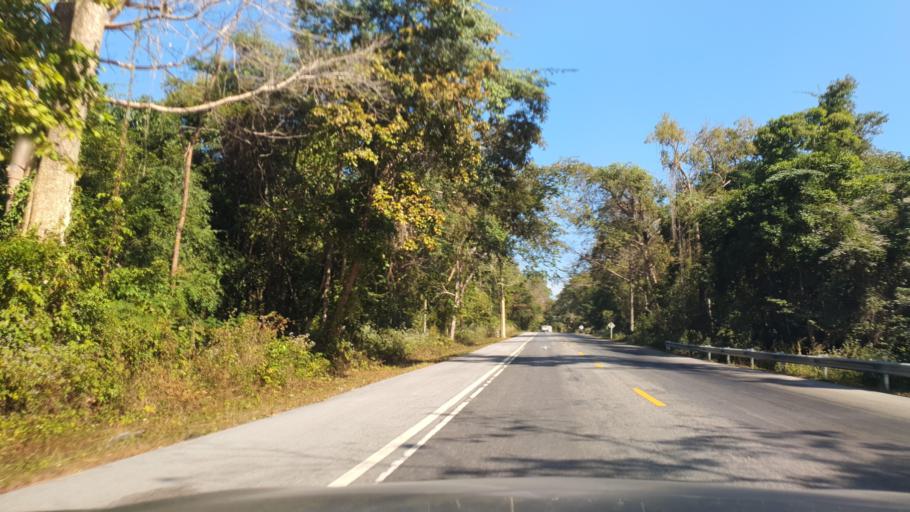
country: TH
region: Kalasin
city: Na Khu
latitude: 16.8485
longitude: 103.9237
